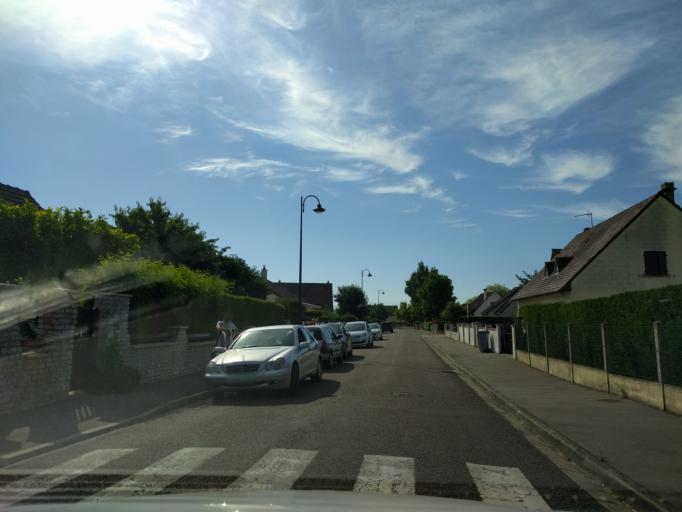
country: FR
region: Picardie
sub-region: Departement de l'Oise
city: Tille
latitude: 49.4669
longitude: 2.1109
